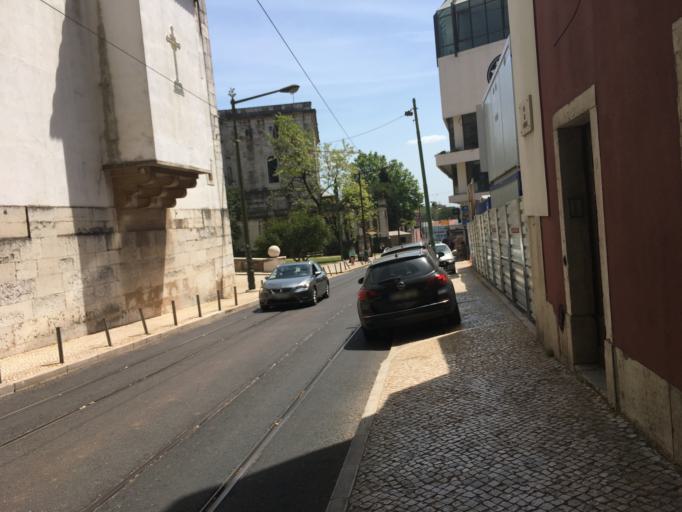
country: PT
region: Lisbon
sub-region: Lisbon
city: Lisbon
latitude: 38.7219
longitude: -9.1569
